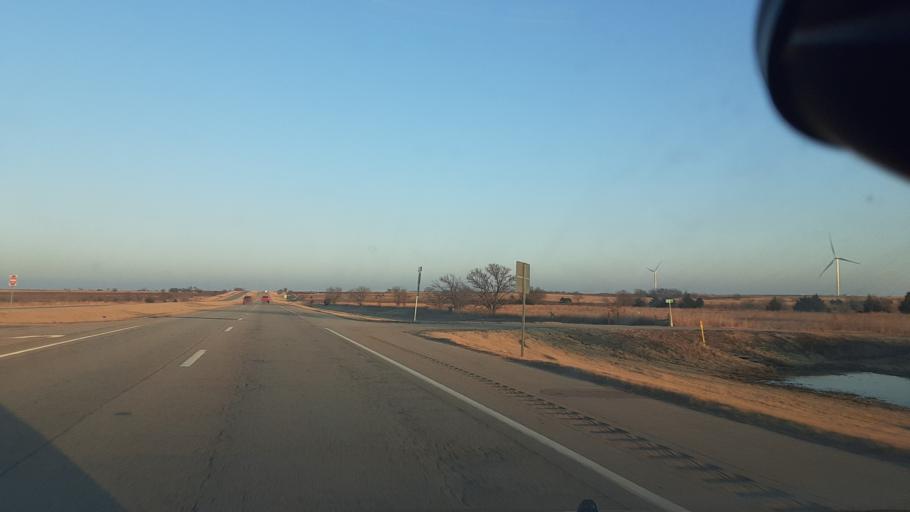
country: US
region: Oklahoma
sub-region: Noble County
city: Perry
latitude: 36.3980
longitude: -97.3908
